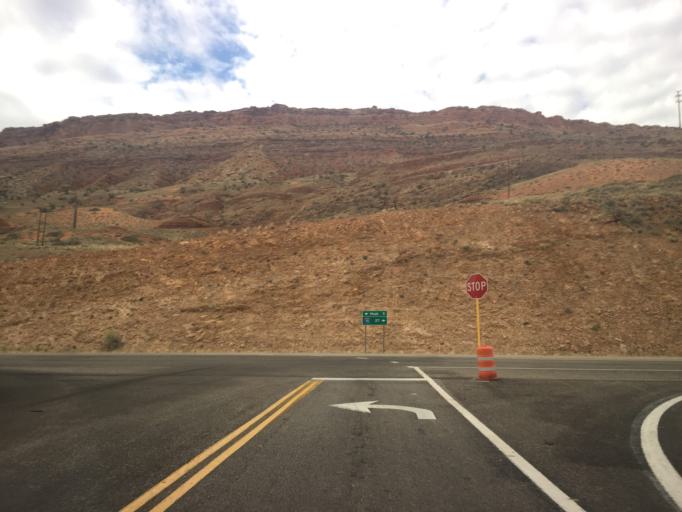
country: US
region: Utah
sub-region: Grand County
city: Moab
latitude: 38.6112
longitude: -109.6080
